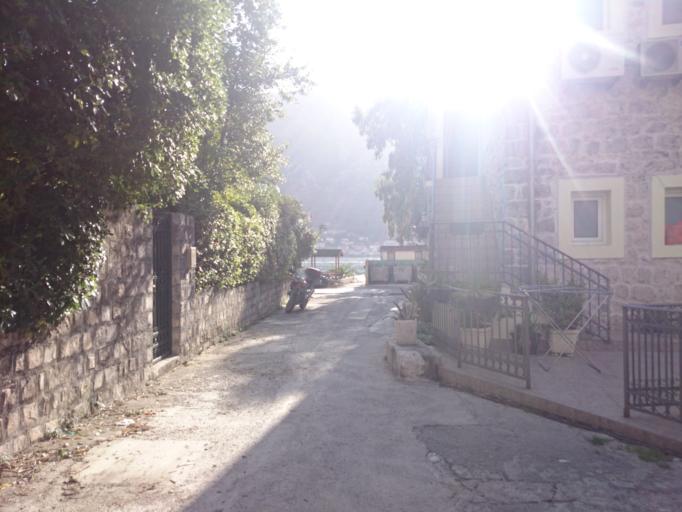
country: ME
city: Dobrota
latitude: 42.4391
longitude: 18.7638
